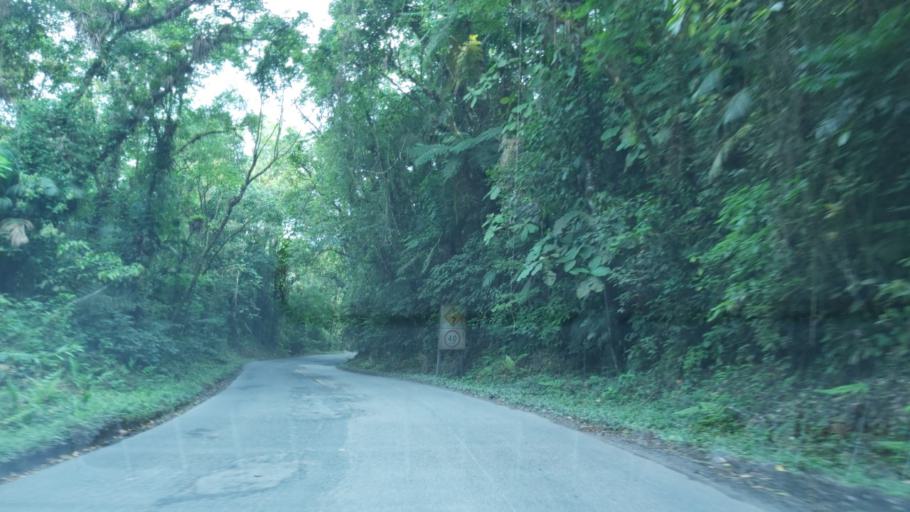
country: BR
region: Sao Paulo
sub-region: Juquia
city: Juquia
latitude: -24.0797
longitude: -47.6065
